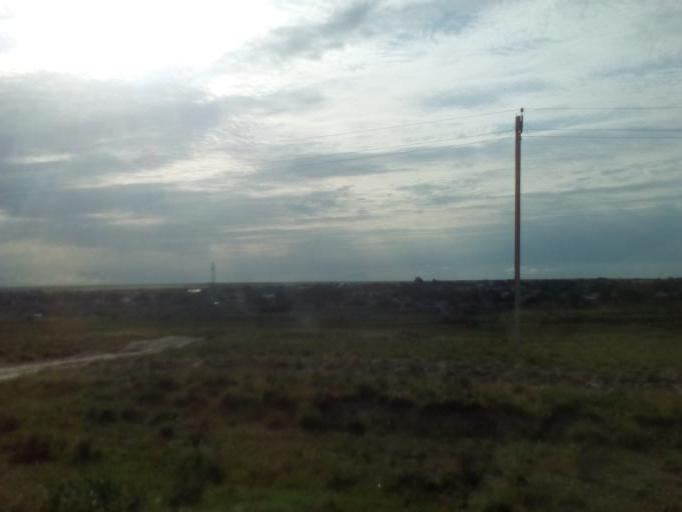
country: KZ
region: Ongtustik Qazaqstan
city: Shayan
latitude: 43.0279
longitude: 69.3936
